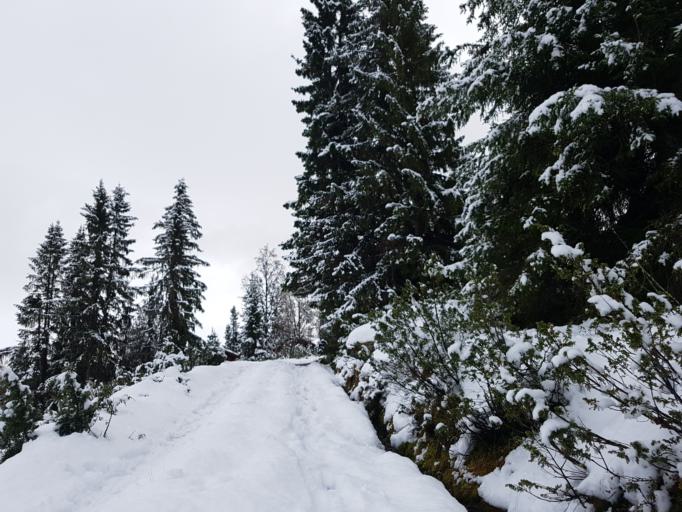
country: NO
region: Oppland
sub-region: Sel
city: Otta
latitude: 61.8069
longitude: 9.6772
